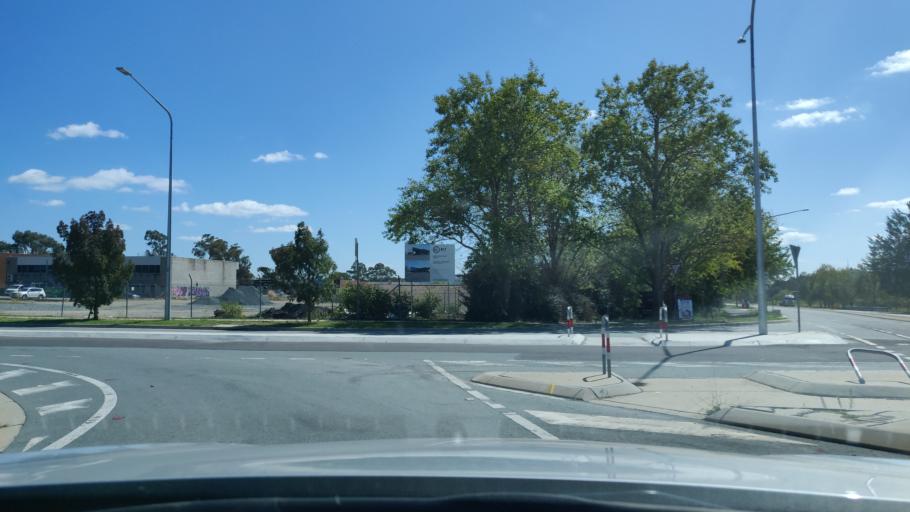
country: AU
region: Australian Capital Territory
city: Forrest
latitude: -35.3550
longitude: 149.0913
